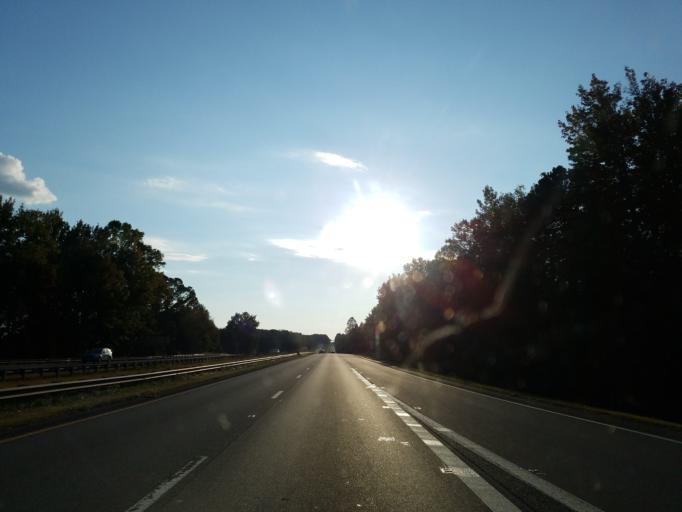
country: US
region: North Carolina
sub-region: Cleveland County
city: White Plains
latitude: 35.1991
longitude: -81.3735
